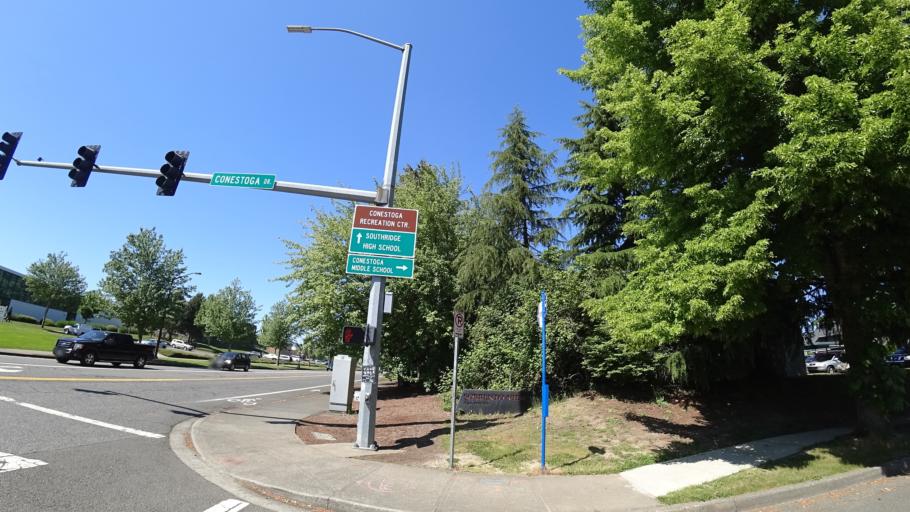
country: US
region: Oregon
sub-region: Washington County
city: Tigard
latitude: 45.4477
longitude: -122.8052
